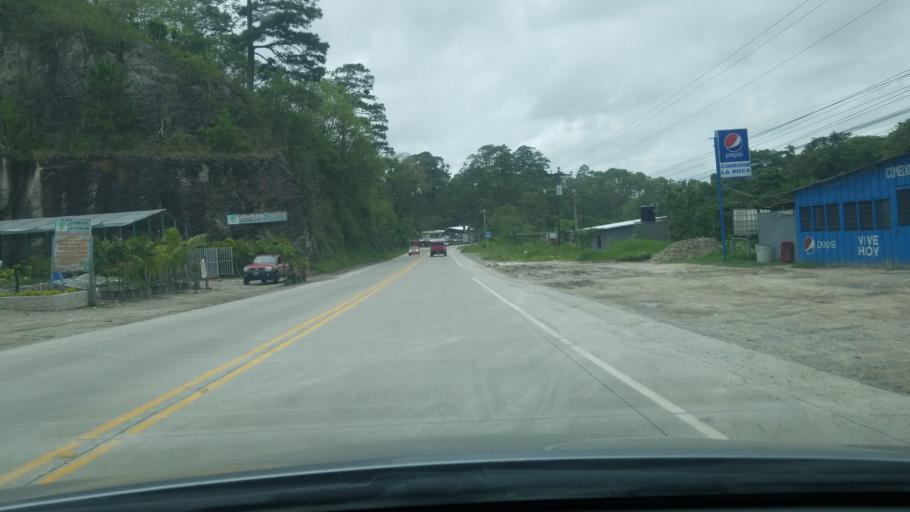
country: HN
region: Copan
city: Santa Rosa de Copan
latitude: 14.8067
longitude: -88.7749
